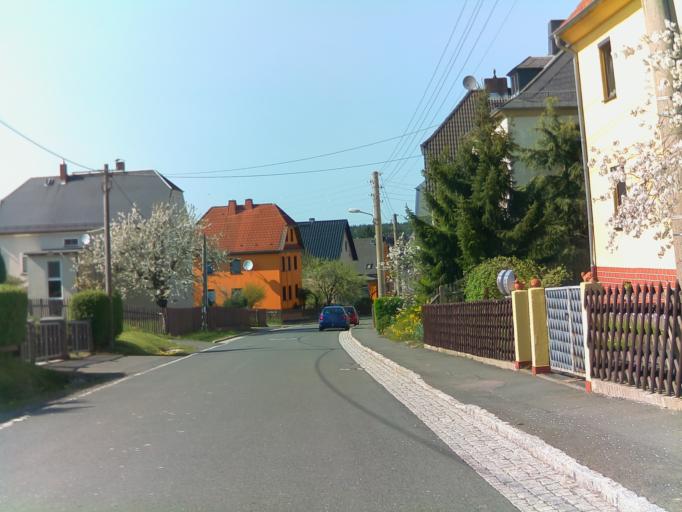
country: DE
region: Saxony
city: Pausa
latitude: 50.6213
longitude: 12.0374
